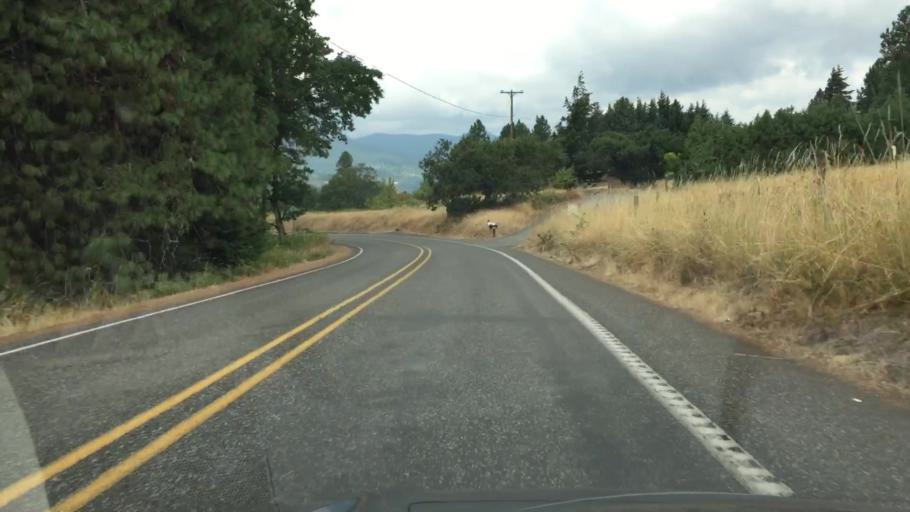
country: US
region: Washington
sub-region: Klickitat County
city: White Salmon
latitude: 45.7324
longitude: -121.5069
